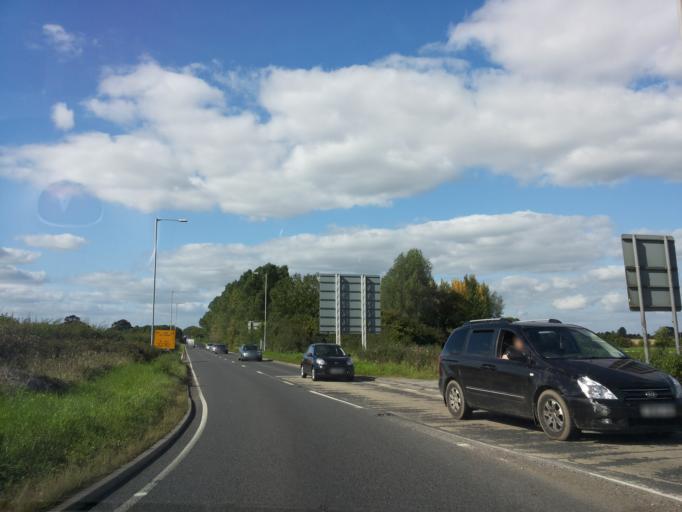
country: GB
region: England
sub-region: Wiltshire
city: Upton Scudamore
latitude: 51.2180
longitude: -2.2020
